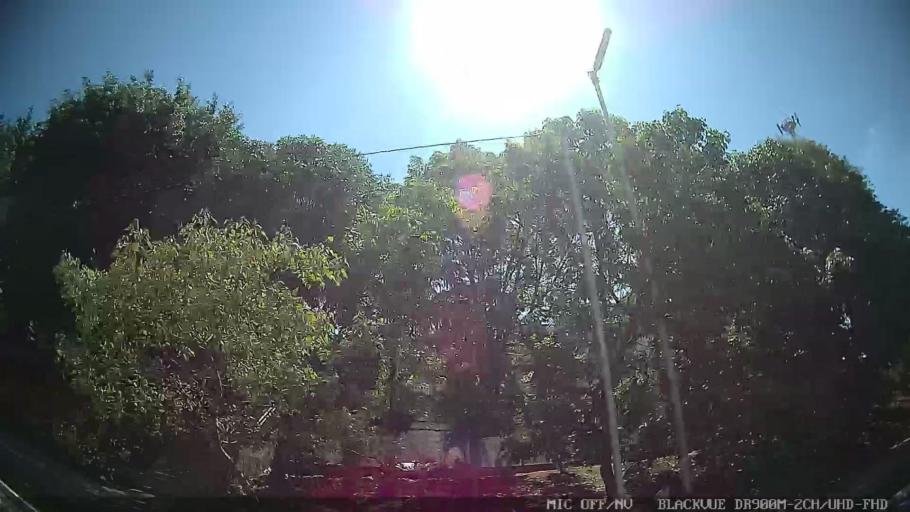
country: BR
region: Sao Paulo
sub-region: Sao Caetano Do Sul
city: Sao Caetano do Sul
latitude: -23.5919
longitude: -46.5069
